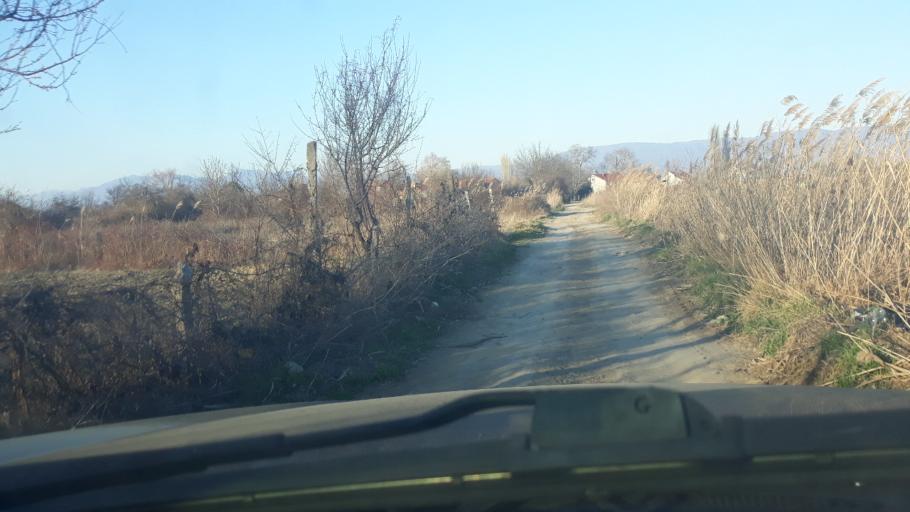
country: MK
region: Strumica
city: Strumica
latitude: 41.4437
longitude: 22.6271
